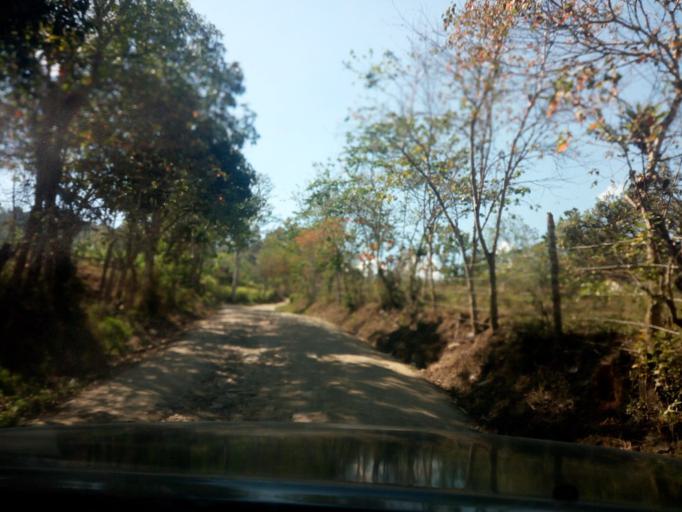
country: CO
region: Boyaca
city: Guateque
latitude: 4.9974
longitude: -73.4658
